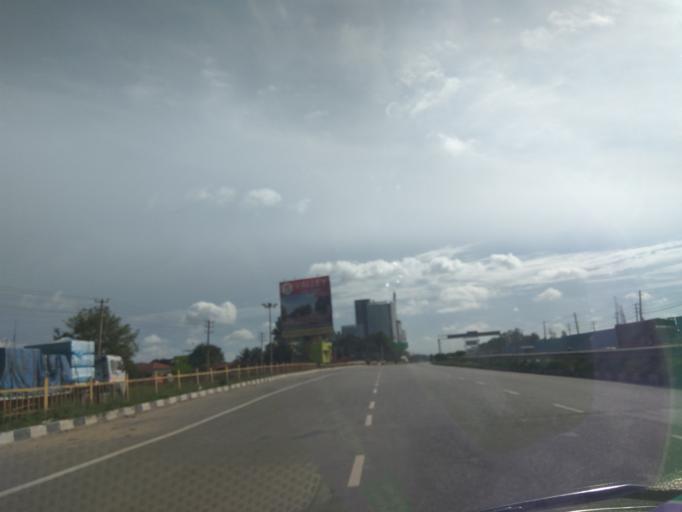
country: IN
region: Karnataka
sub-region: Bangalore Rural
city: Hoskote
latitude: 13.0502
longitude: 77.7560
